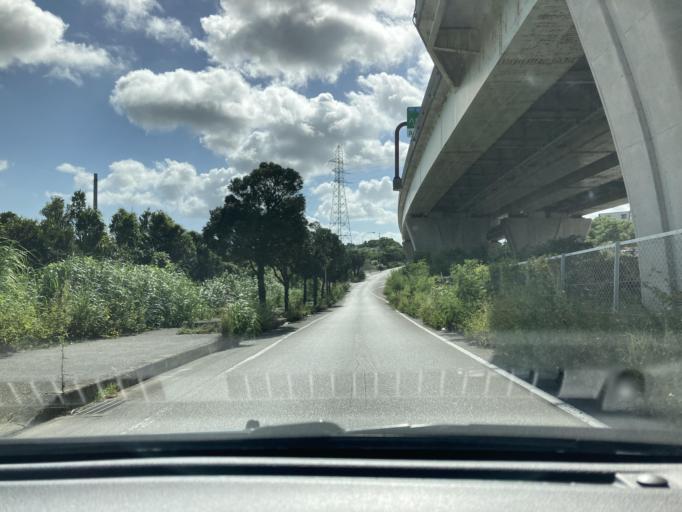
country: JP
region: Okinawa
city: Tomigusuku
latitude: 26.1830
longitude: 127.7339
